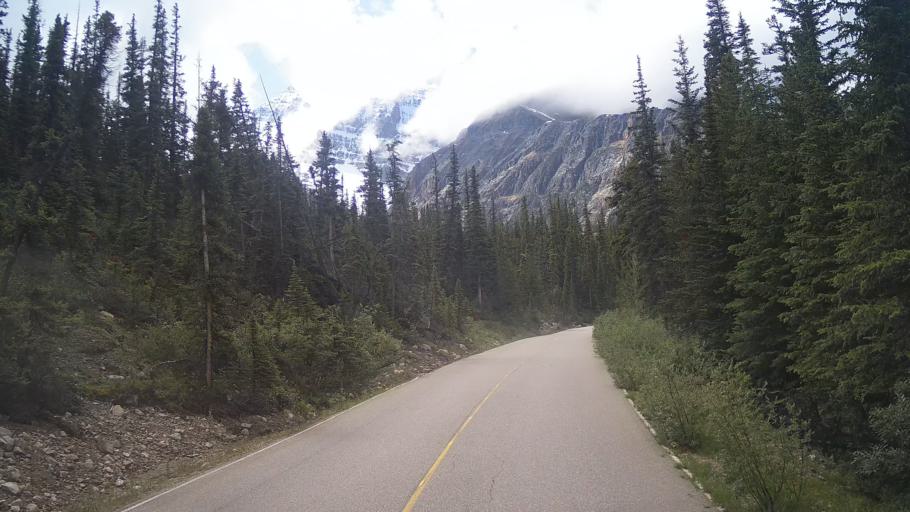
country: CA
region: Alberta
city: Jasper Park Lodge
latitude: 52.7064
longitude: -118.0583
